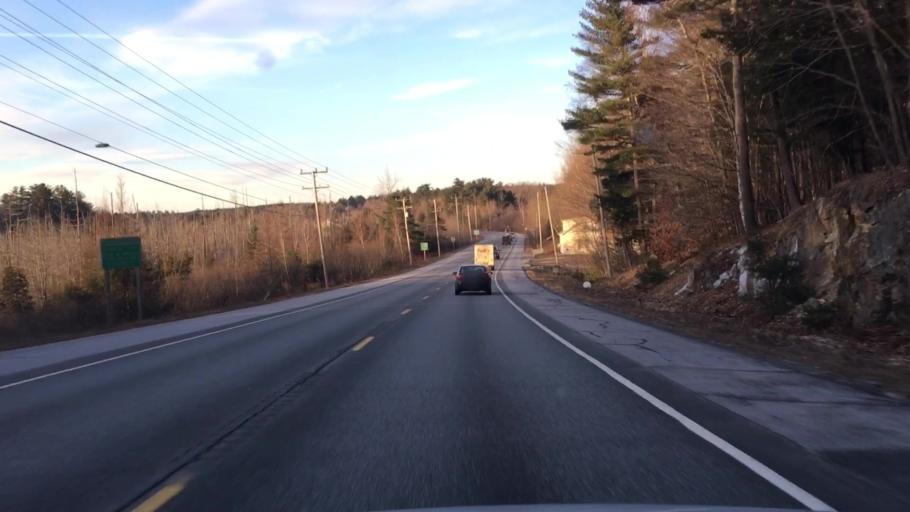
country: US
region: Maine
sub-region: Hancock County
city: Dedham
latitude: 44.7302
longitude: -68.6240
